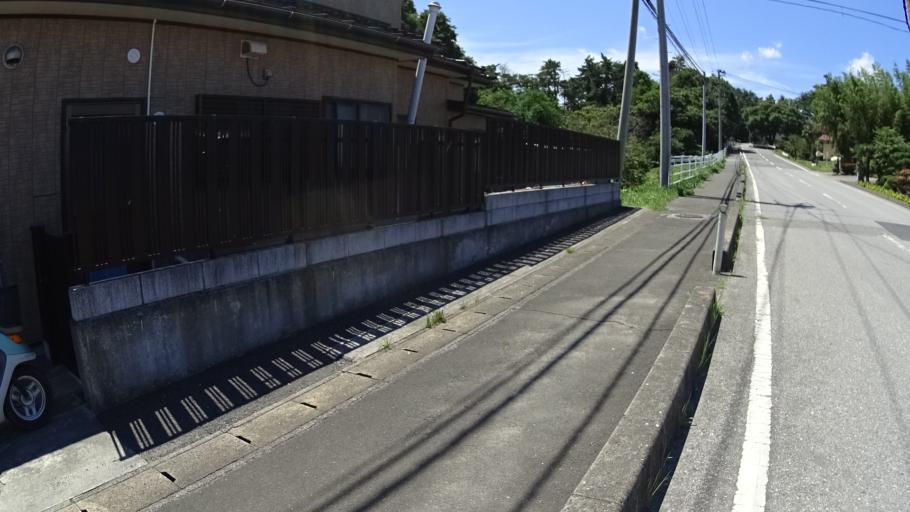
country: JP
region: Iwate
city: Ofunato
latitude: 38.8449
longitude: 141.6307
